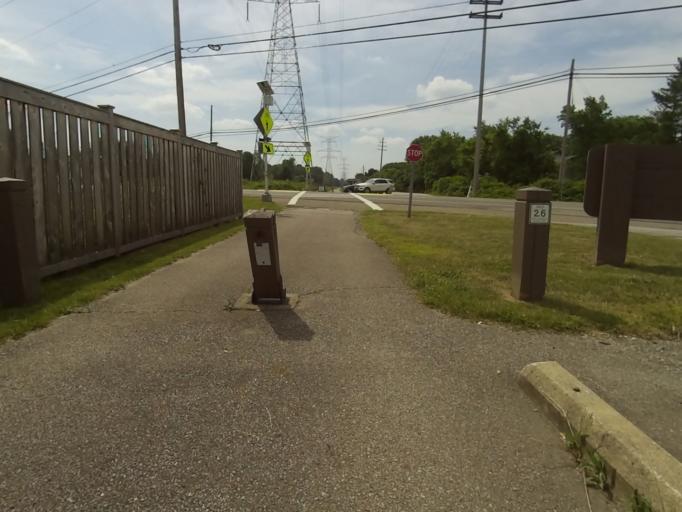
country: US
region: Ohio
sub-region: Summit County
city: Northfield
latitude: 41.3146
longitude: -81.5633
